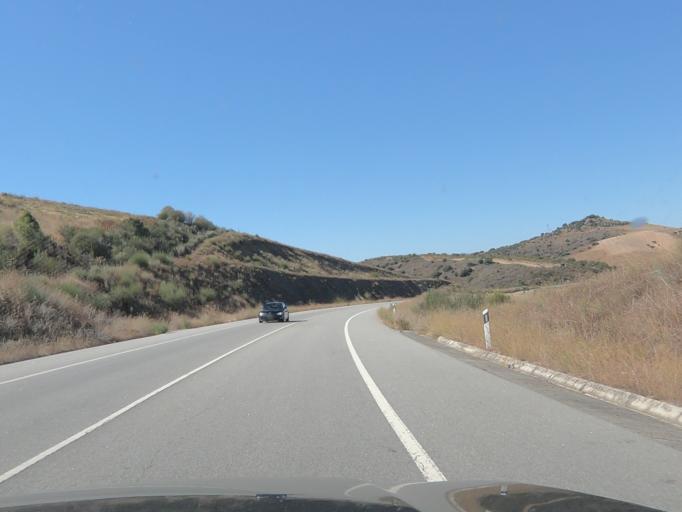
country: PT
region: Braganca
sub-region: Mirandela
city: Mirandela
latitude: 41.5198
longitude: -7.2376
